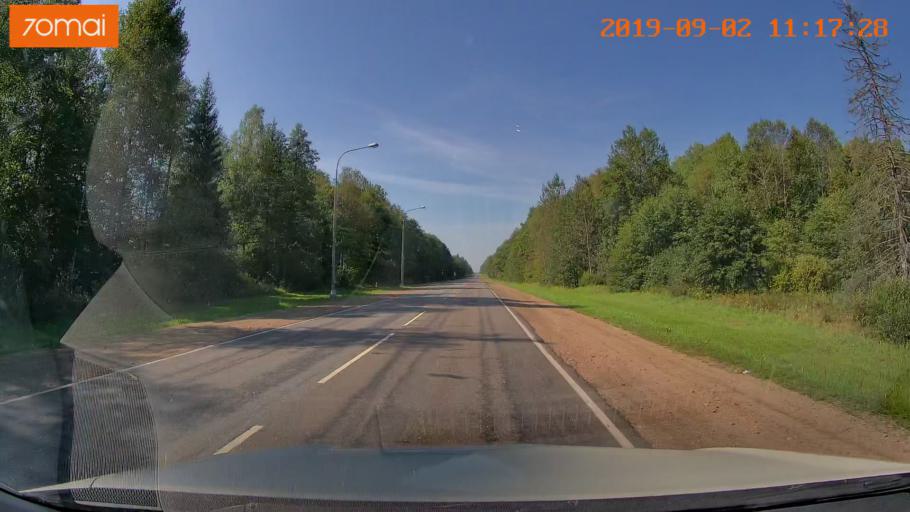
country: RU
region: Smolensk
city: Yekimovichi
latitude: 54.0616
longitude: 33.1181
